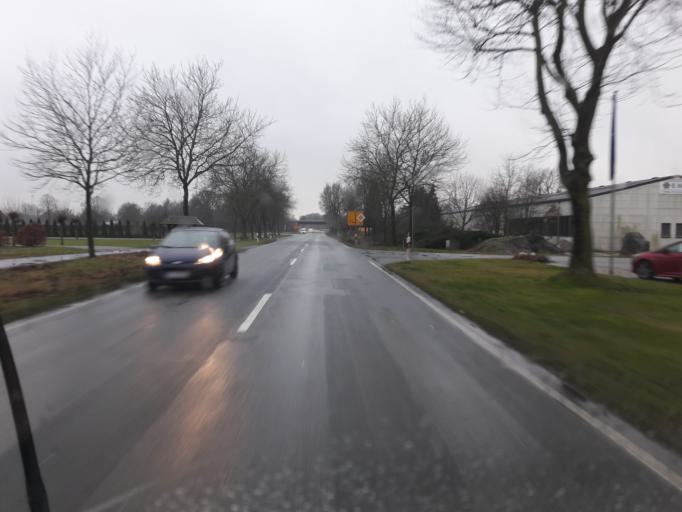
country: DE
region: Lower Saxony
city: Uchte
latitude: 52.4914
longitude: 8.8928
